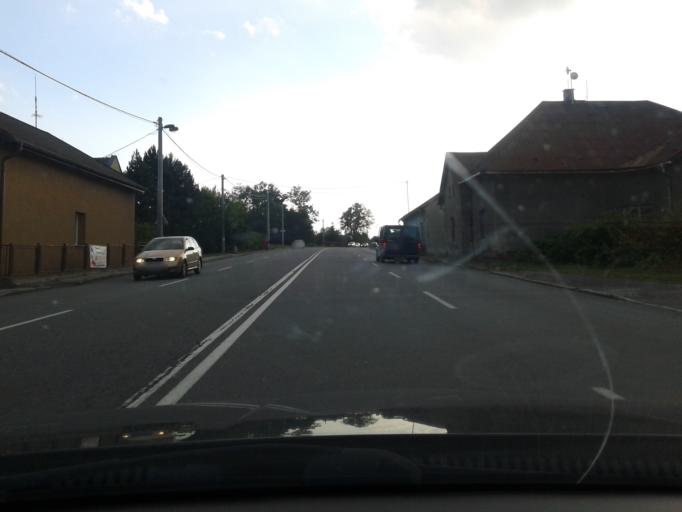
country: CZ
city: Petrvald
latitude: 49.8260
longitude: 18.3722
